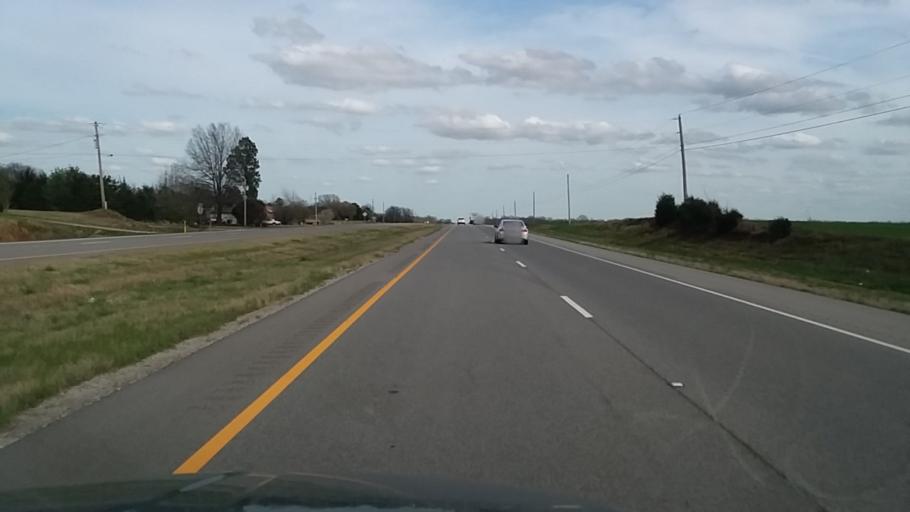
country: US
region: Alabama
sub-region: Colbert County
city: Muscle Shoals
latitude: 34.6846
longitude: -87.5623
